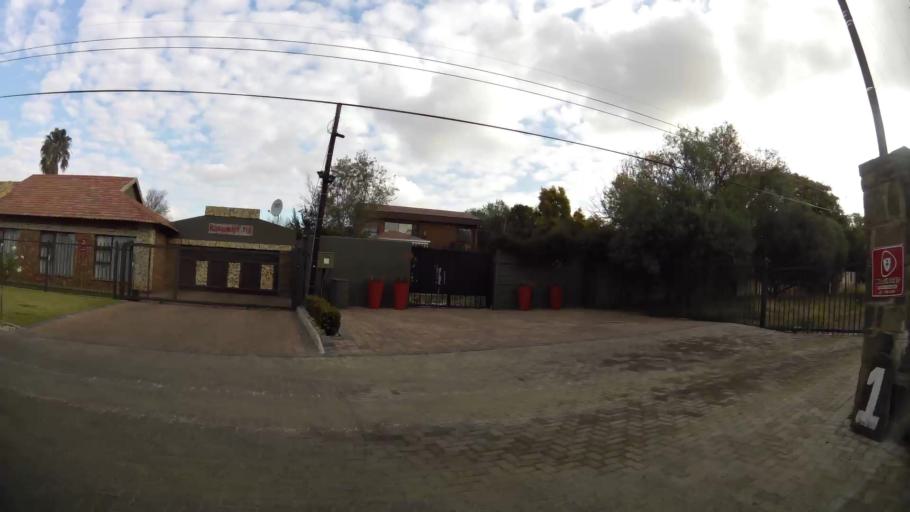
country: ZA
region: Orange Free State
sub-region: Mangaung Metropolitan Municipality
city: Bloemfontein
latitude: -29.0770
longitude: 26.2030
